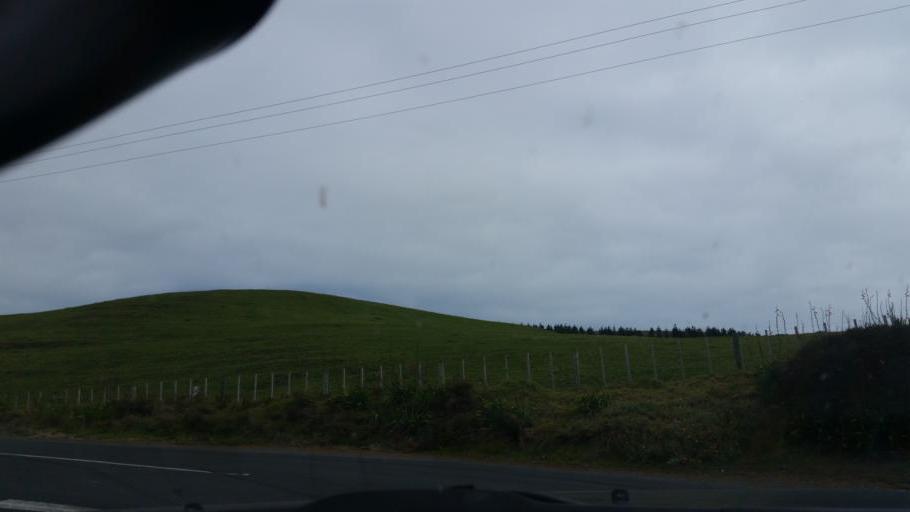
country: NZ
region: Northland
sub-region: Kaipara District
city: Dargaville
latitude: -35.8143
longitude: 173.6418
